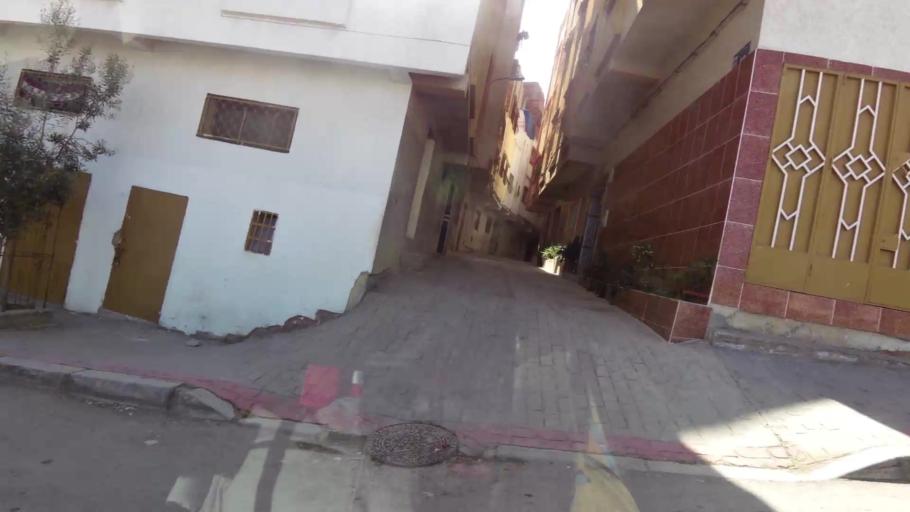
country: MA
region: Tanger-Tetouan
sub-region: Tanger-Assilah
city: Tangier
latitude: 35.7403
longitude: -5.8088
